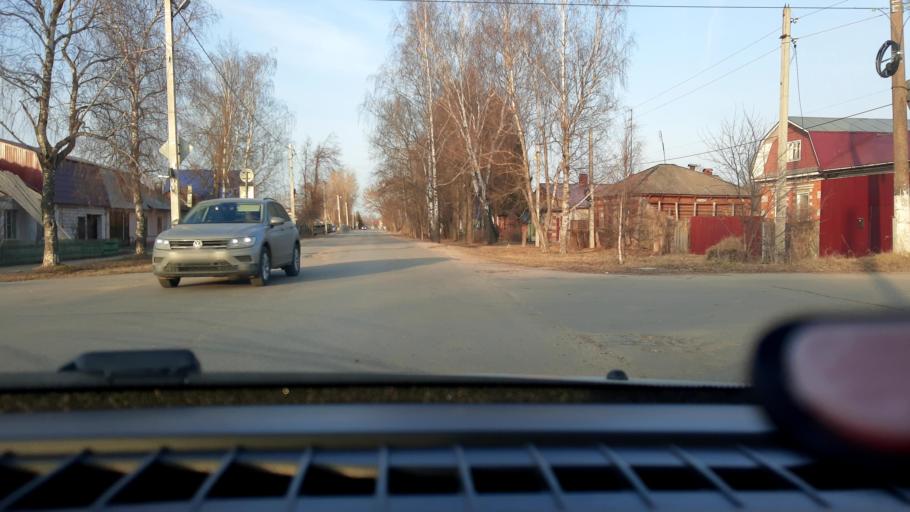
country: RU
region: Nizjnij Novgorod
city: Bogorodsk
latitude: 56.1055
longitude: 43.4903
